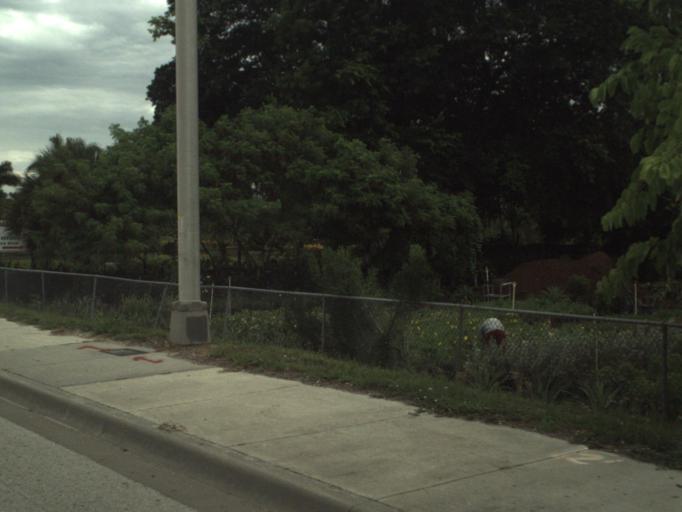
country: US
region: Florida
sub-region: Palm Beach County
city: Lake Belvedere Estates
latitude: 26.6796
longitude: -80.1705
